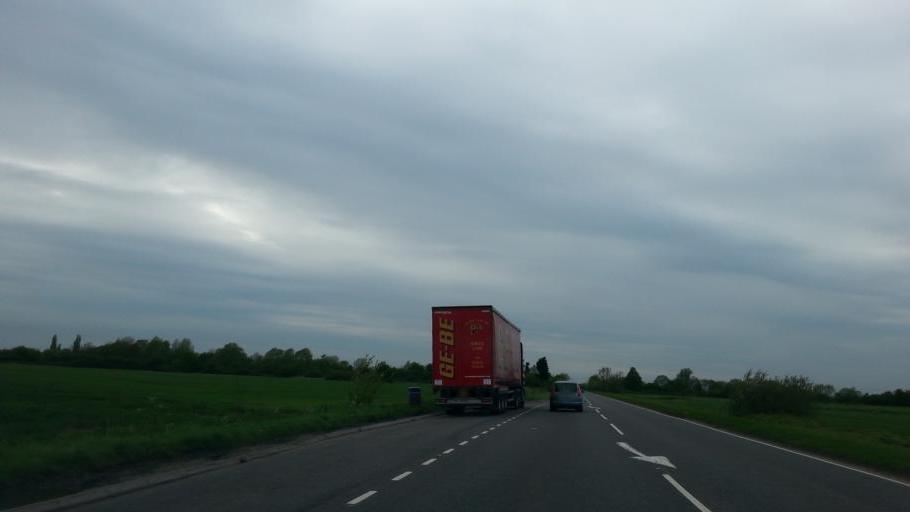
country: GB
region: England
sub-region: Cambridgeshire
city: March
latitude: 52.5260
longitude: 0.0788
